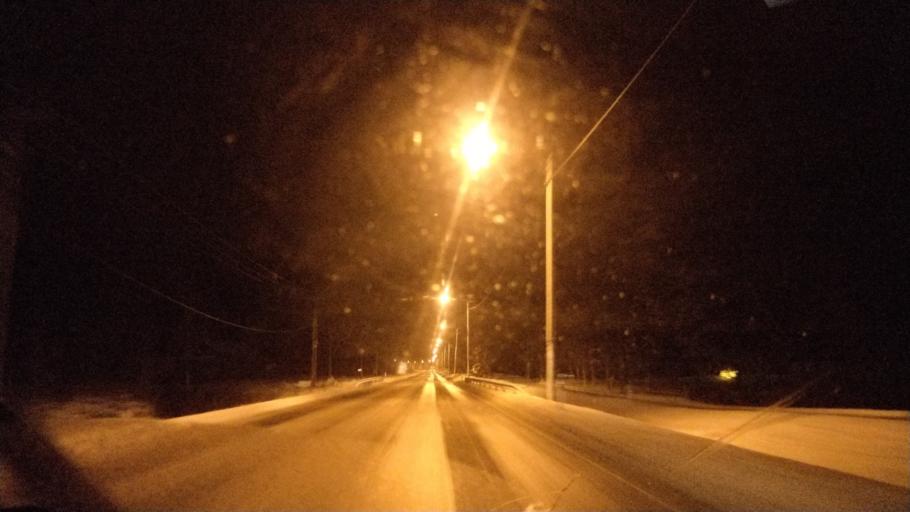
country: FI
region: Lapland
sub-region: Rovaniemi
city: Rovaniemi
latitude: 66.3083
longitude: 25.3600
